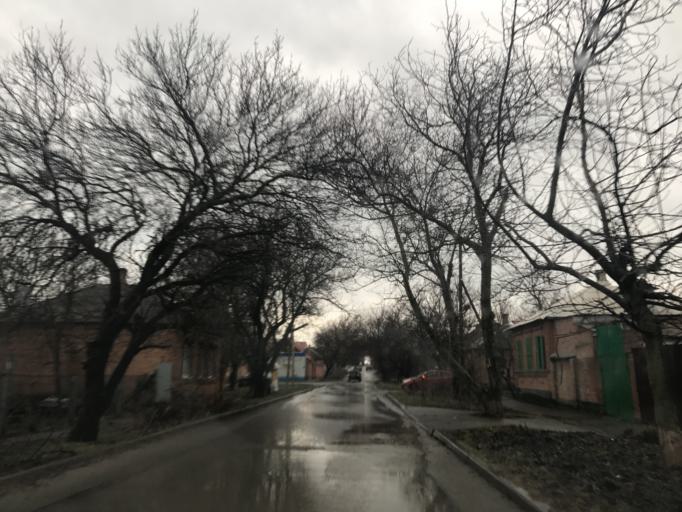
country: RU
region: Rostov
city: Rostov-na-Donu
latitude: 47.2272
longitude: 39.6460
